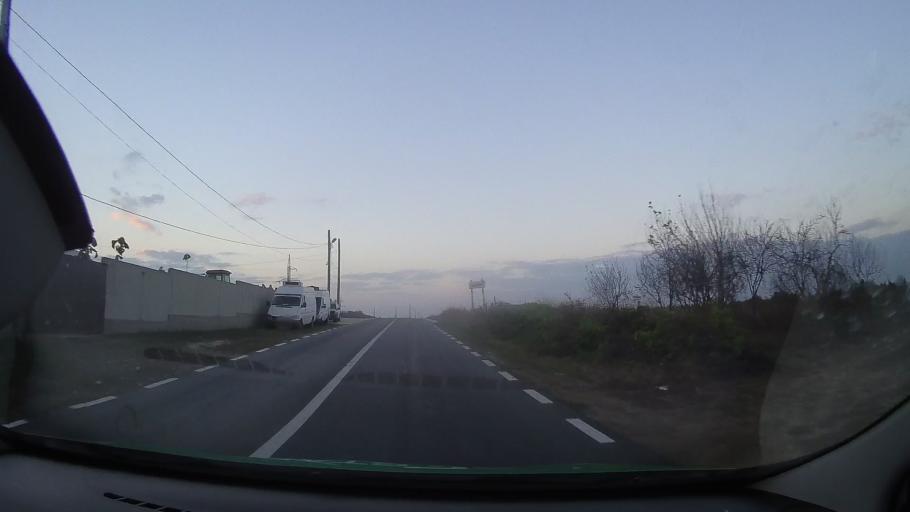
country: RO
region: Constanta
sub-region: Comuna Baneasa
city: Baneasa
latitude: 44.1026
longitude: 27.6749
